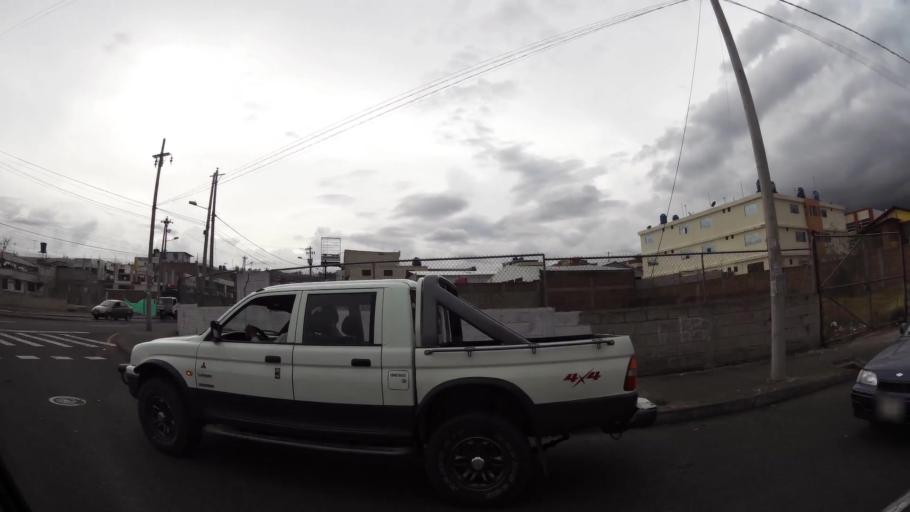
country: EC
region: Tungurahua
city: Ambato
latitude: -1.2760
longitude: -78.6262
